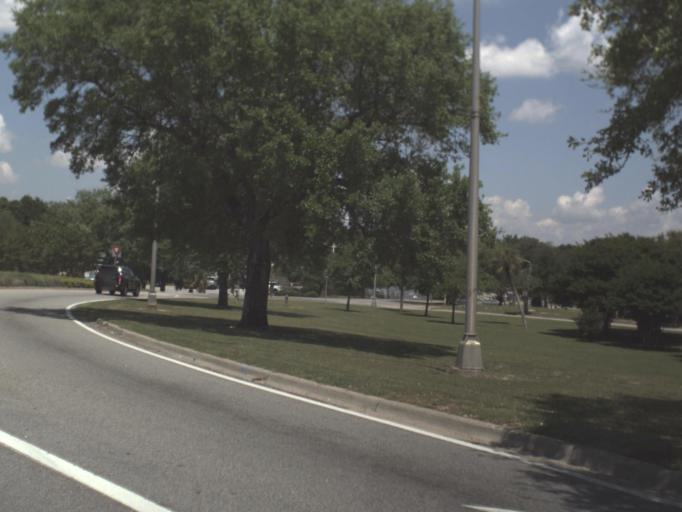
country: US
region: Florida
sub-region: Escambia County
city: East Pensacola Heights
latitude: 30.4175
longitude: -87.1940
